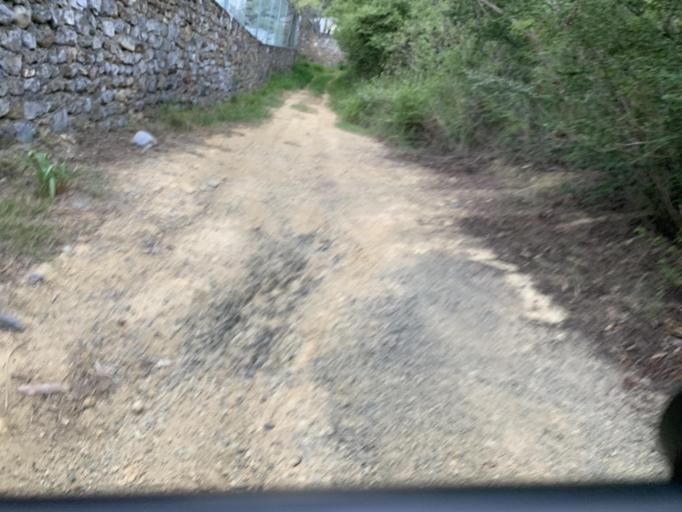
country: MX
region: Nuevo Leon
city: Santiago
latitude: 25.5050
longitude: -100.1821
